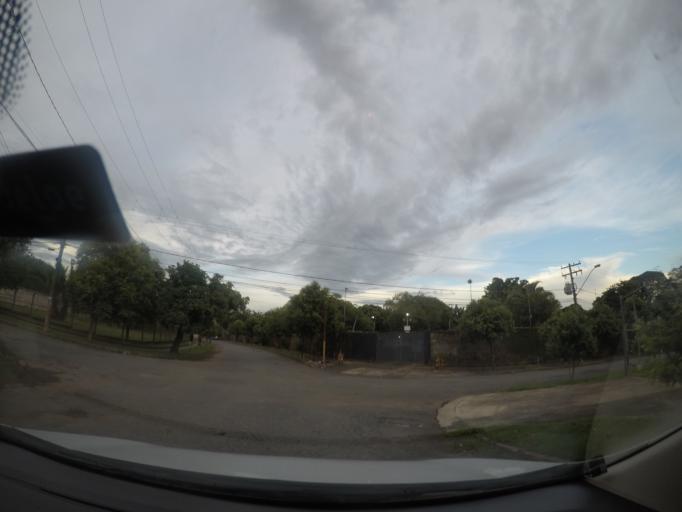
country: BR
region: Goias
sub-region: Goiania
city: Goiania
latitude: -16.6515
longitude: -49.2242
